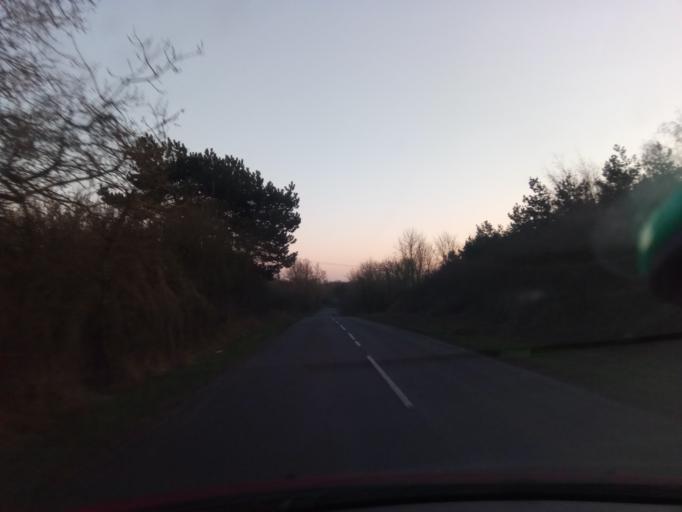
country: GB
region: England
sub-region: Leicestershire
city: Sileby
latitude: 52.7601
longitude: -1.1014
